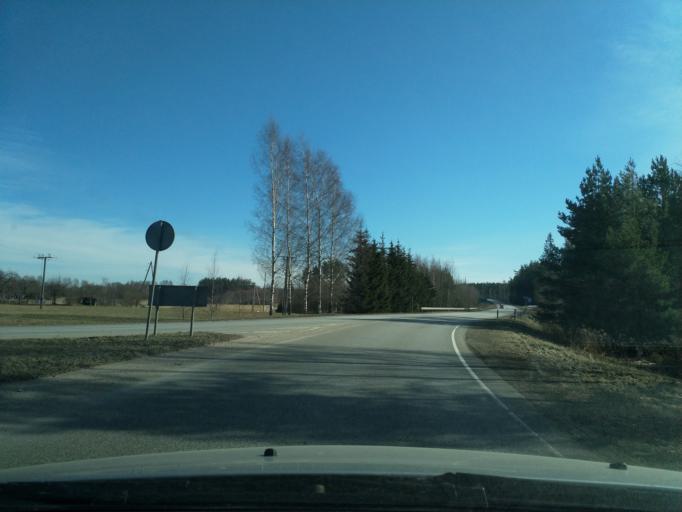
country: LV
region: Valmieras Rajons
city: Valmiera
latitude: 57.5119
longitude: 25.4237
